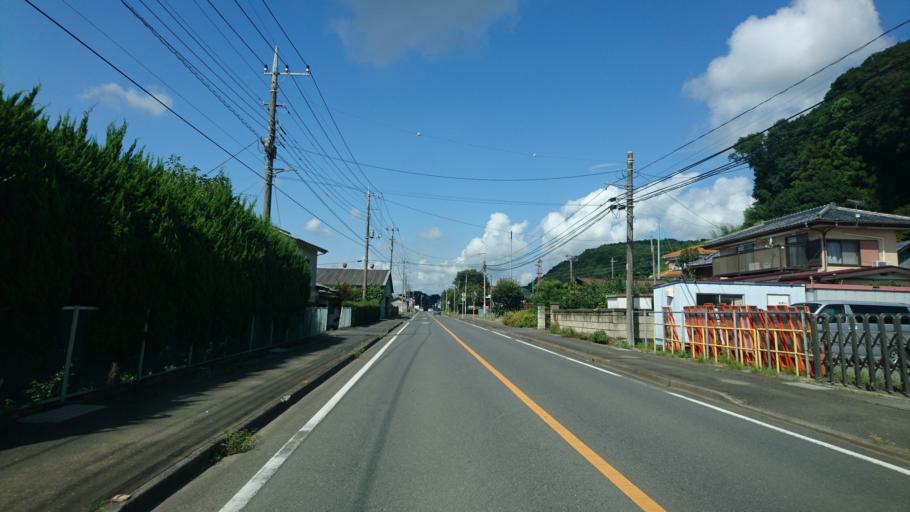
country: JP
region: Gunma
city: Omamacho-omama
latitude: 36.4344
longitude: 139.2877
